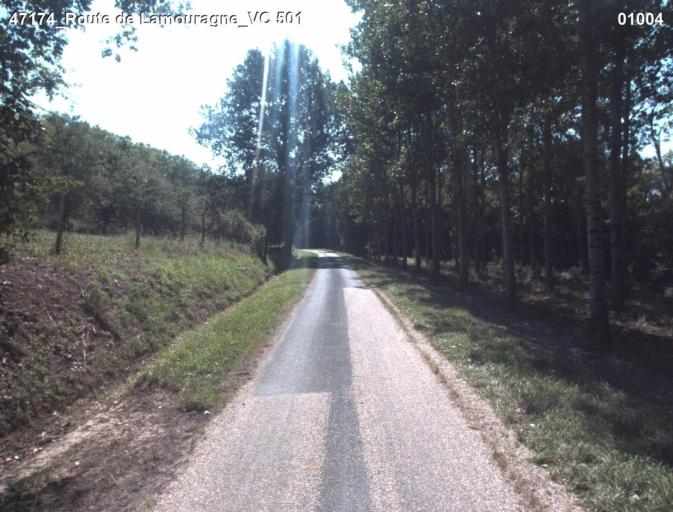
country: FR
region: Midi-Pyrenees
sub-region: Departement du Gers
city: Condom
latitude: 44.0389
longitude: 0.3879
